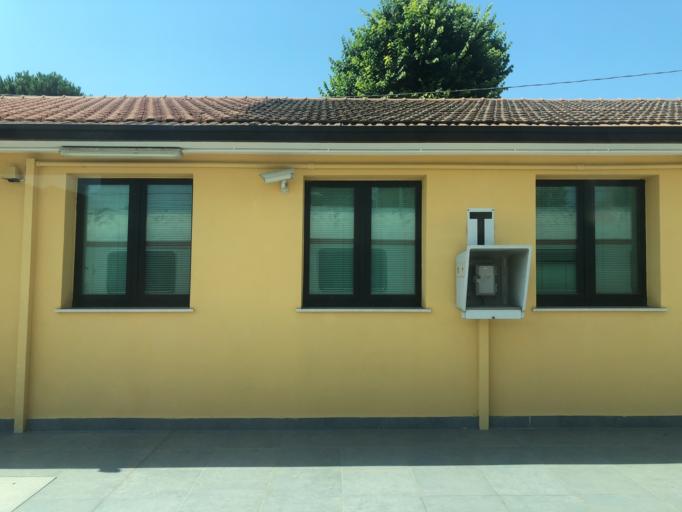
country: IT
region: Emilia-Romagna
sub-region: Provincia di Ravenna
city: Castel Bolognese
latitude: 44.3251
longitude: 11.8050
